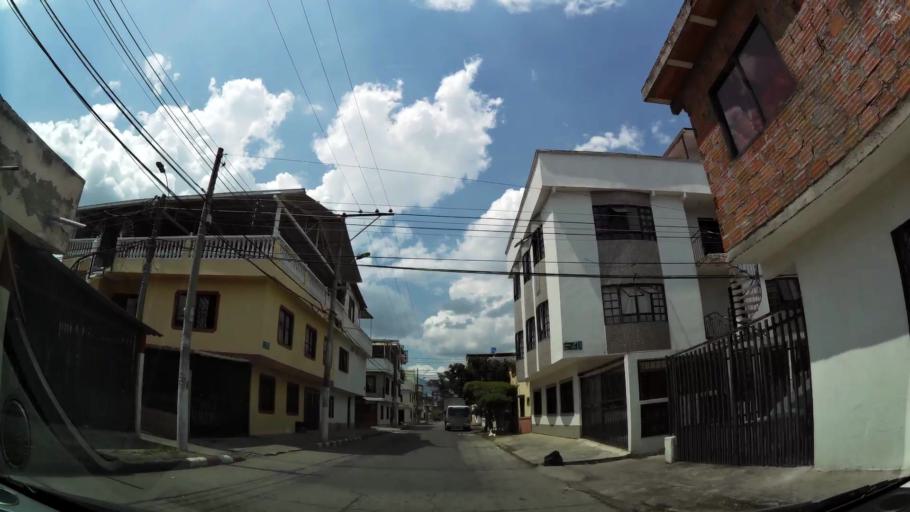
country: CO
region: Valle del Cauca
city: Cali
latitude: 3.4632
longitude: -76.5038
